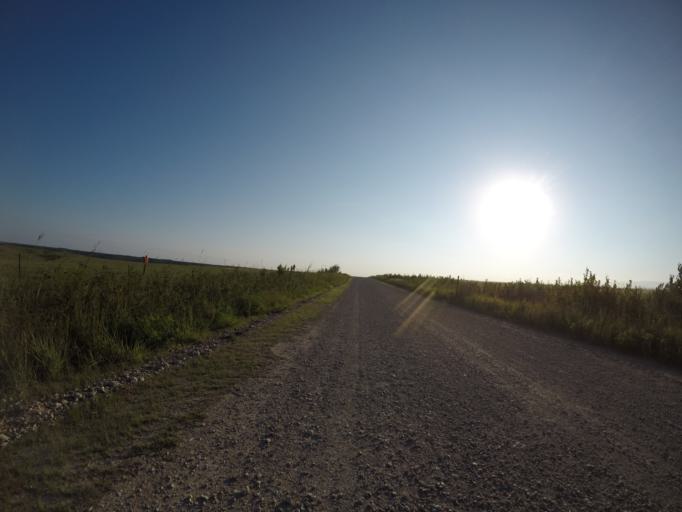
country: US
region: Kansas
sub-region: Riley County
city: Ogden
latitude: 39.0467
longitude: -96.6976
